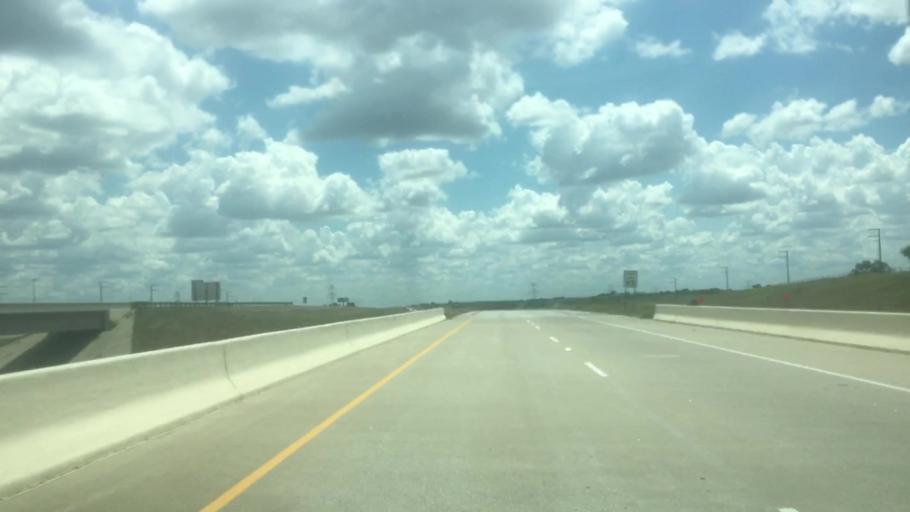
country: US
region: Texas
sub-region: Caldwell County
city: Uhland
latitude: 30.0052
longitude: -97.6875
